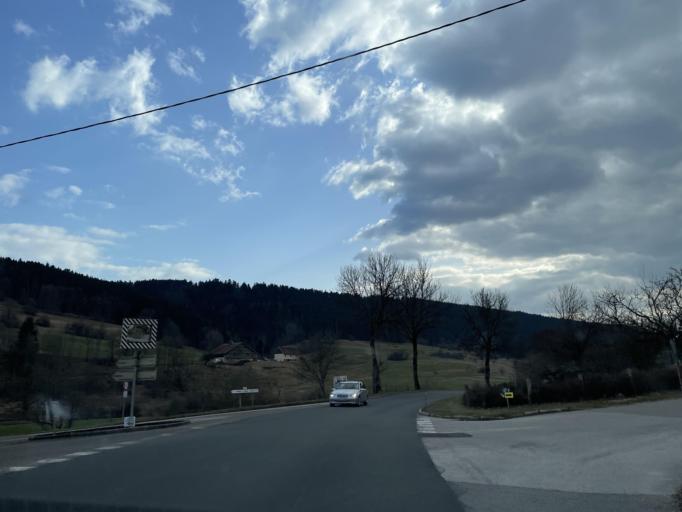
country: FR
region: Franche-Comte
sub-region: Departement du Doubs
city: Gilley
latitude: 47.0032
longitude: 6.4786
